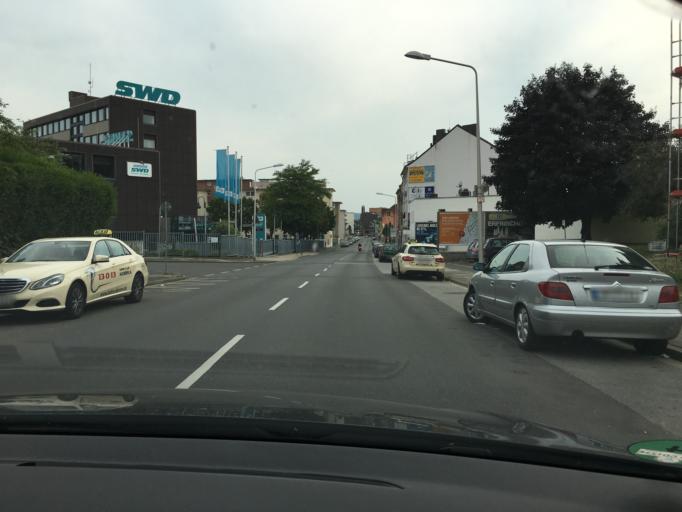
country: DE
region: North Rhine-Westphalia
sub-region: Regierungsbezirk Koln
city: Dueren
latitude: 50.8116
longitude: 6.4879
